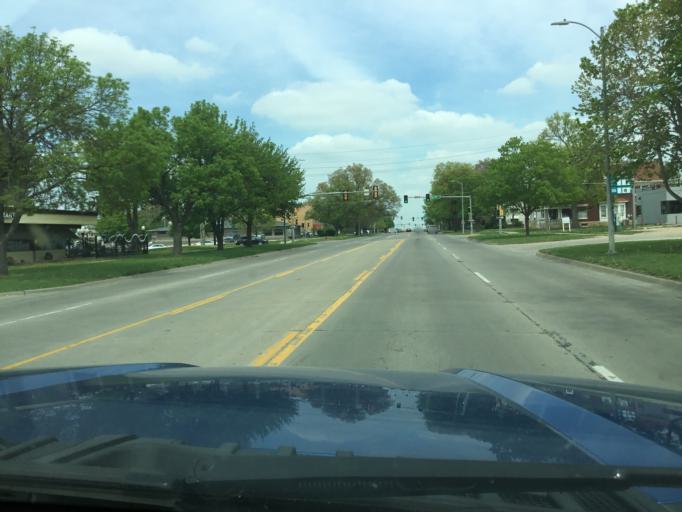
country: US
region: Kansas
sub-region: Shawnee County
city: Topeka
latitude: 39.0539
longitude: -95.6787
